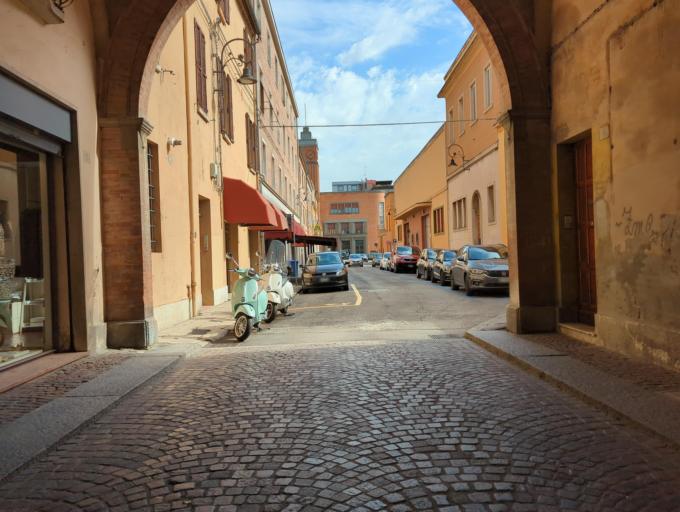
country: IT
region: Emilia-Romagna
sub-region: Provincia di Ferrara
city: Ferrara
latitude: 44.8389
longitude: 11.6209
